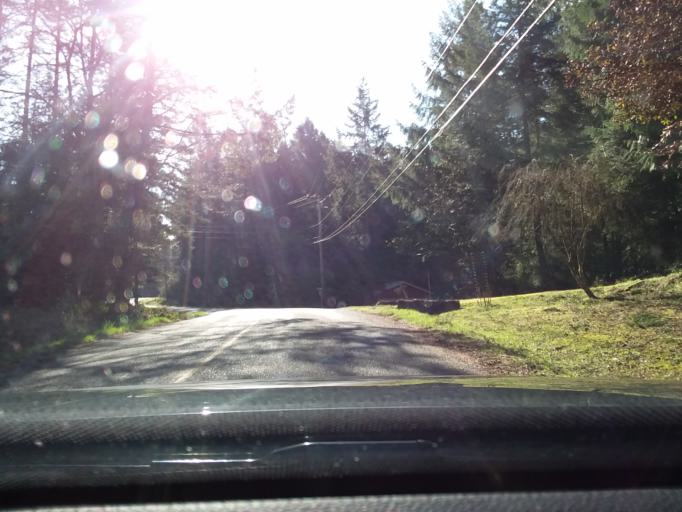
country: CA
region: British Columbia
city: North Cowichan
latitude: 48.9395
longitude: -123.4937
